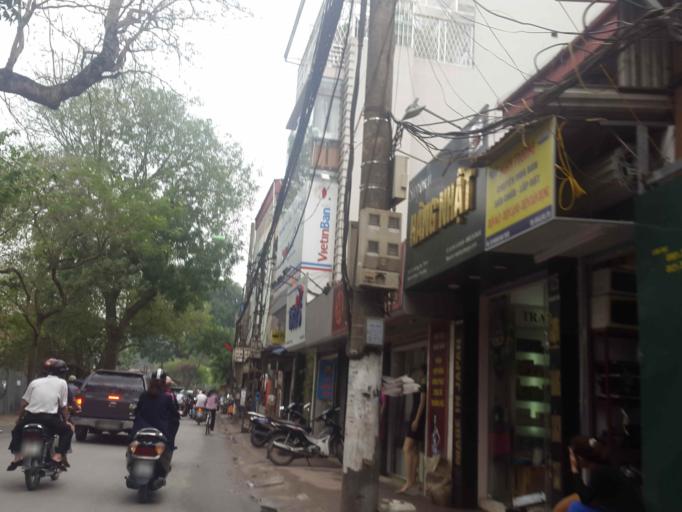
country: VN
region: Ha Noi
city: Dong Da
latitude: 21.0404
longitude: 105.8255
